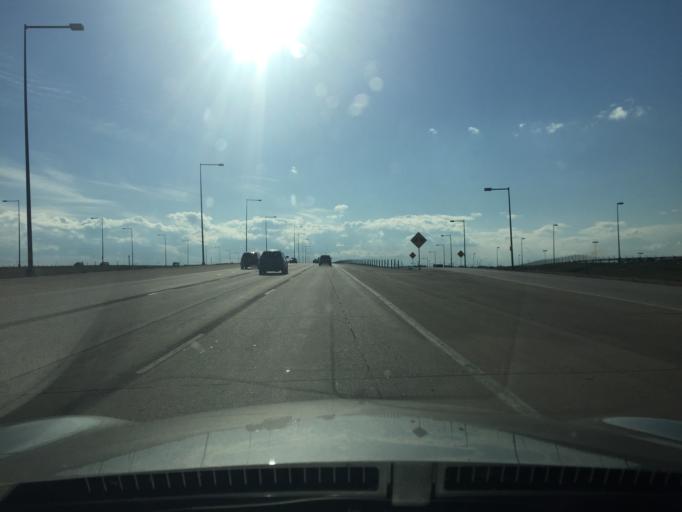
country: US
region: Colorado
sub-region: Weld County
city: Lochbuie
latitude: 39.8343
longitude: -104.6884
